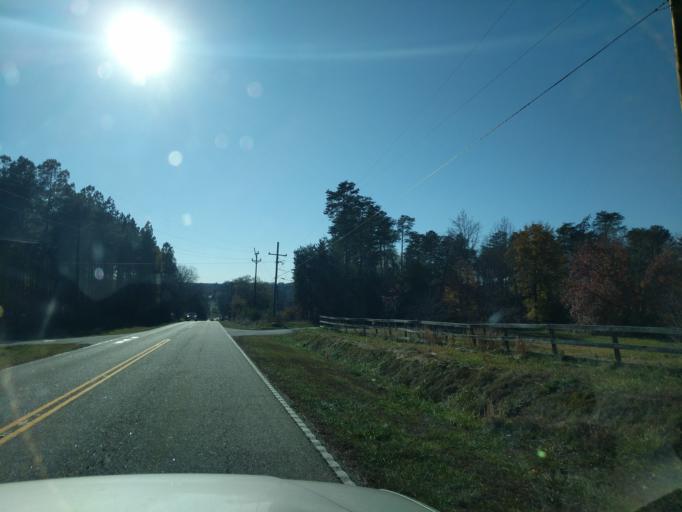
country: US
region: South Carolina
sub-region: Spartanburg County
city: Landrum
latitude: 35.1253
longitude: -82.1378
